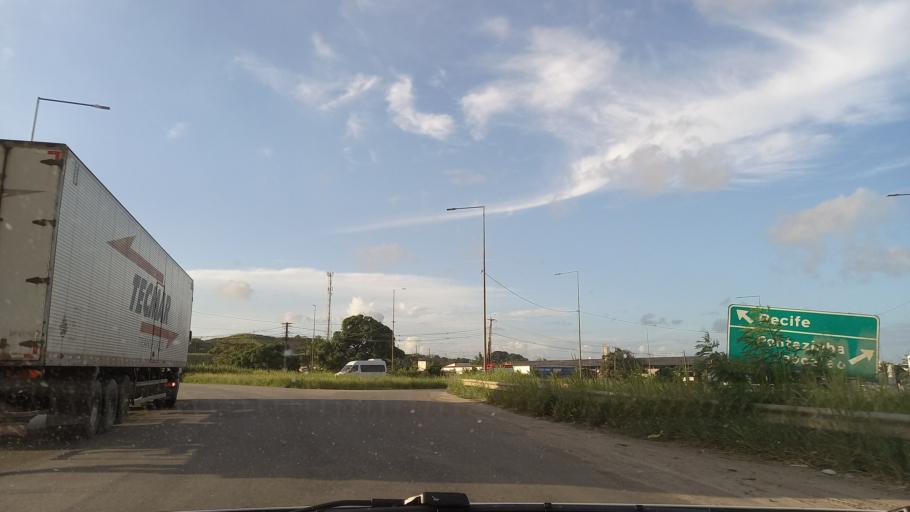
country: BR
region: Pernambuco
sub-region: Cabo De Santo Agostinho
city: Cabo
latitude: -8.2513
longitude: -35.0055
